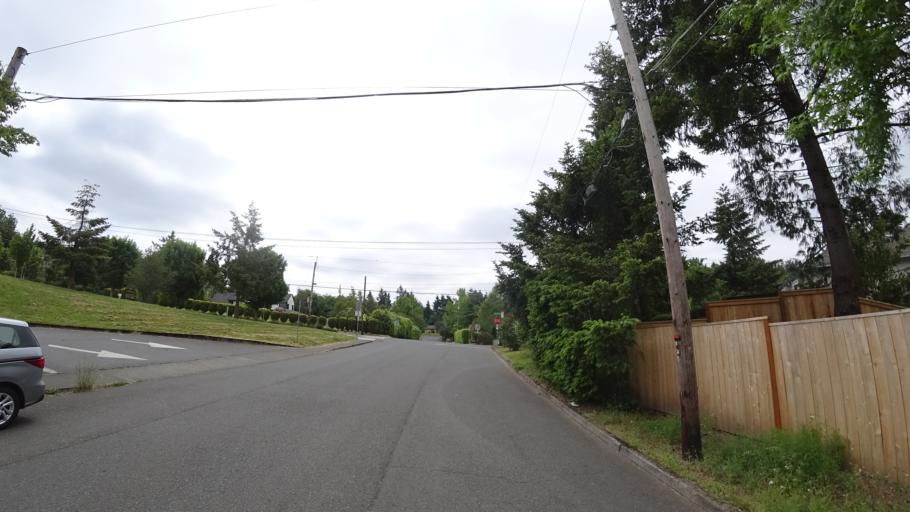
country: US
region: Oregon
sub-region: Clackamas County
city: Lake Oswego
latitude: 45.4406
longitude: -122.7051
